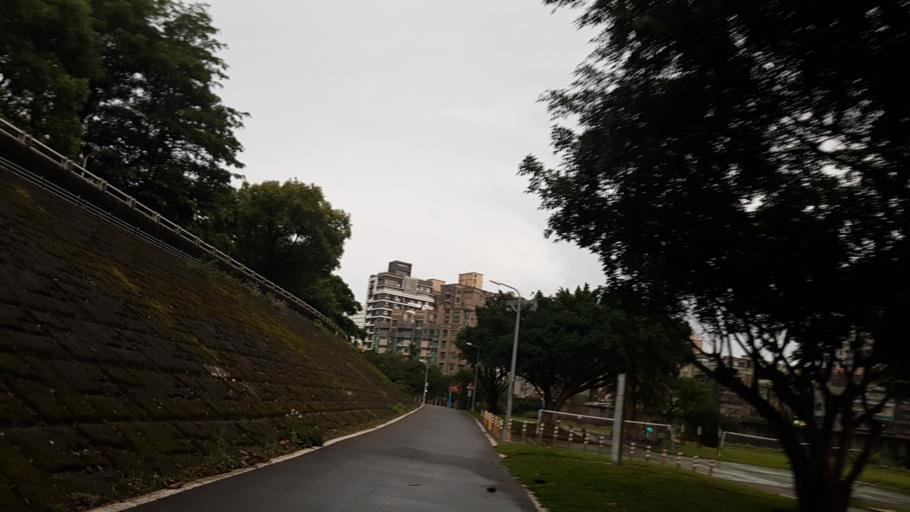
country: TW
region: Taipei
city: Taipei
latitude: 24.9853
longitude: 121.5451
